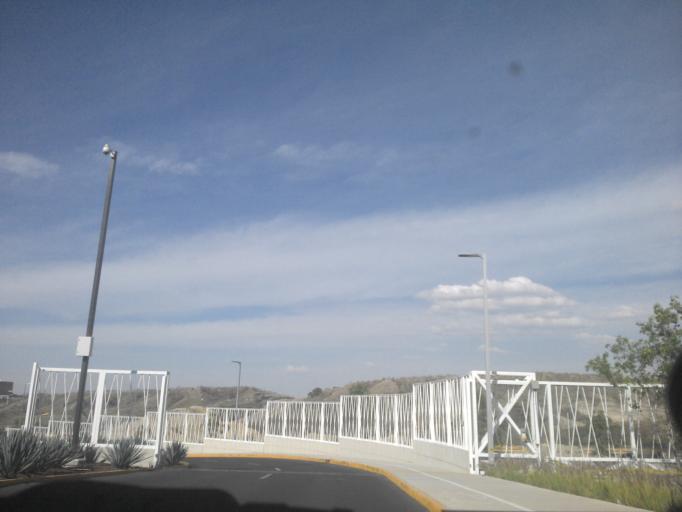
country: MX
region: Jalisco
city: Guadalajara
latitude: 20.6710
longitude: -103.4632
